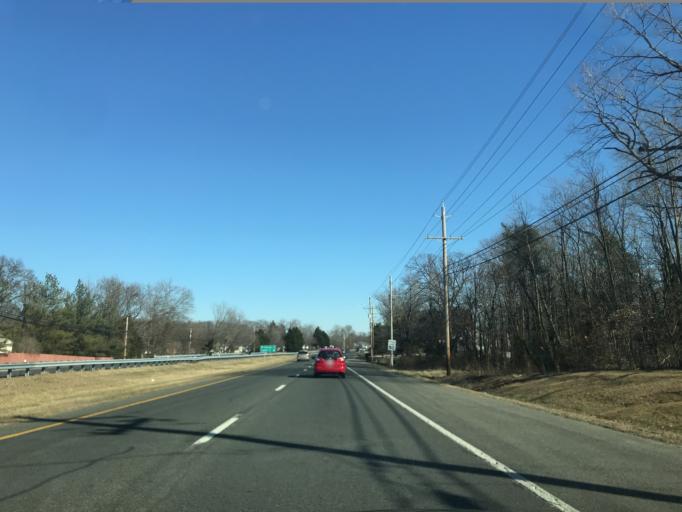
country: US
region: Maryland
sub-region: Charles County
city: Waldorf
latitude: 38.6489
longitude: -76.9479
